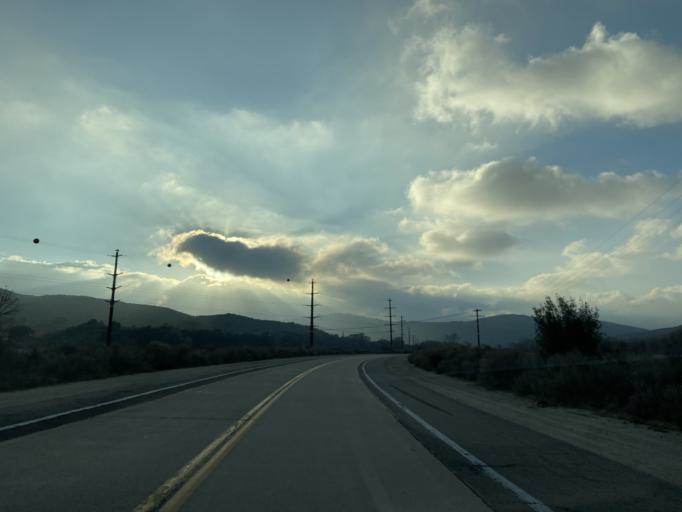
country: US
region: California
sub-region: San Diego County
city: Campo
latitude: 32.7186
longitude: -116.4516
